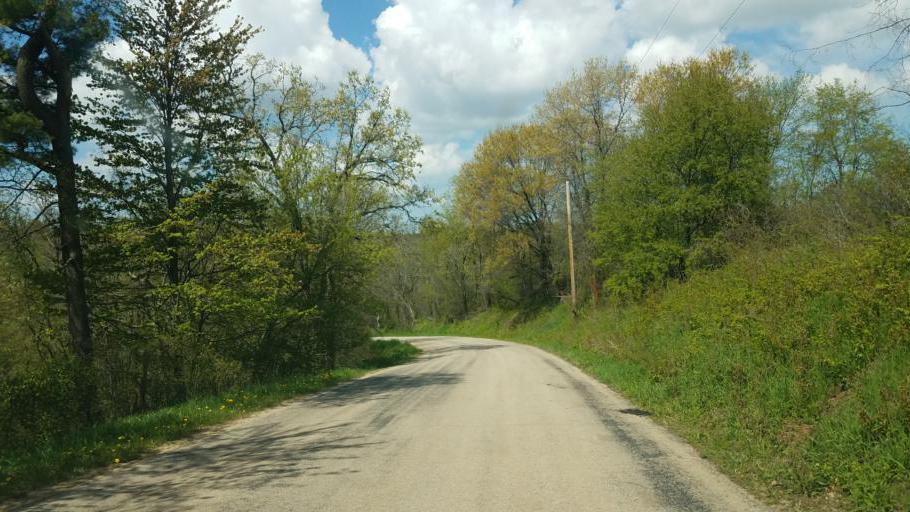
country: US
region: Wisconsin
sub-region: Juneau County
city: Elroy
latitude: 43.6954
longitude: -90.2953
